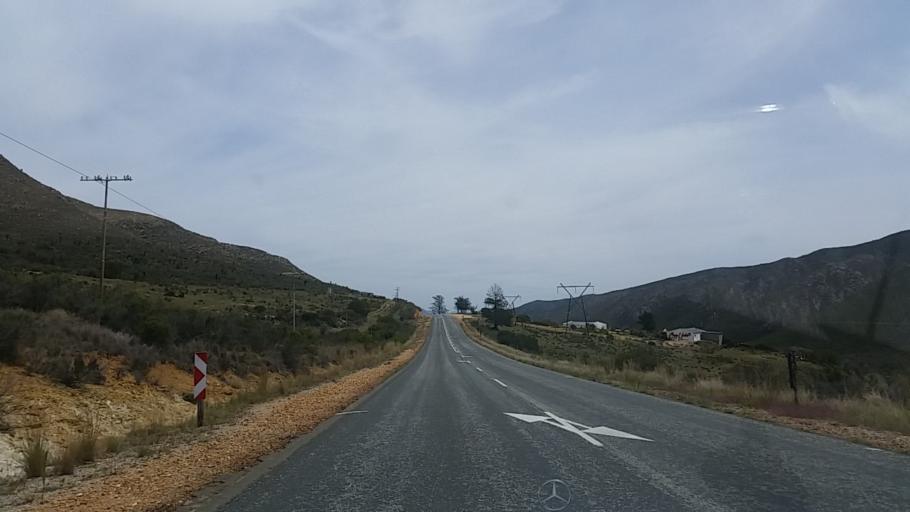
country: ZA
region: Western Cape
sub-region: Eden District Municipality
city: Knysna
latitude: -33.7439
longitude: 22.9952
